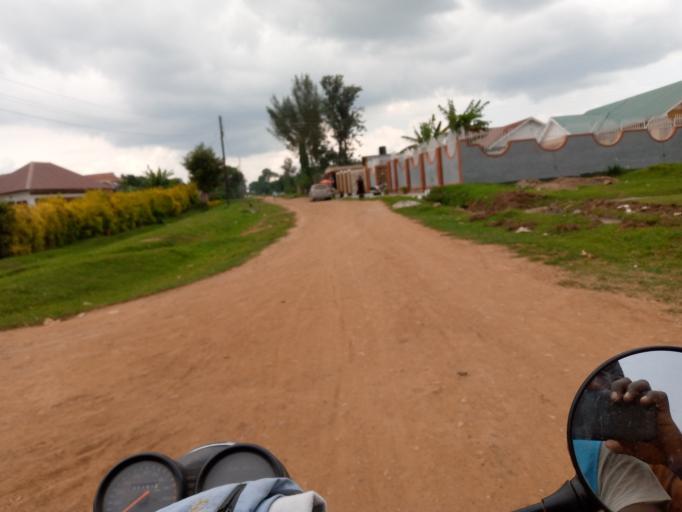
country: UG
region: Eastern Region
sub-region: Mbale District
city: Mbale
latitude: 1.0865
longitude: 34.1706
